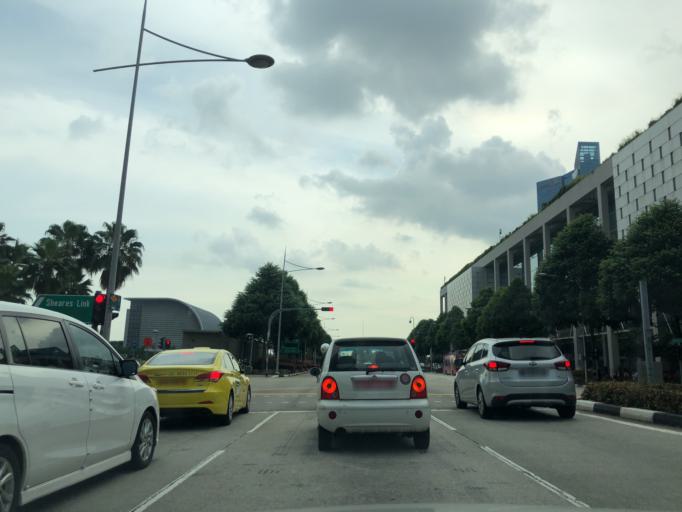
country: SG
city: Singapore
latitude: 1.2826
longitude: 103.8598
